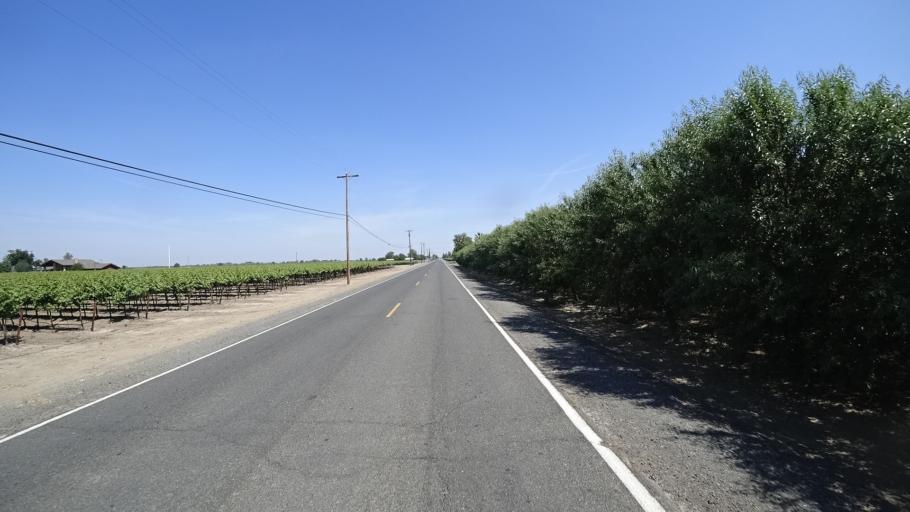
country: US
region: California
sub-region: Fresno County
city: Riverdale
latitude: 36.3635
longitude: -119.8513
